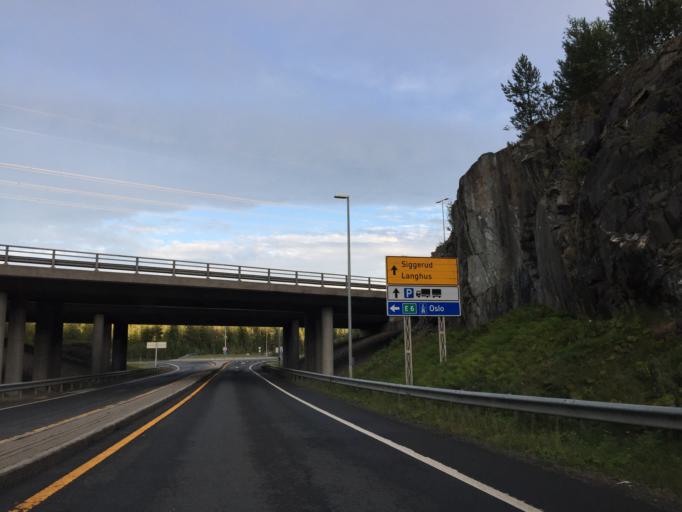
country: NO
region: Akershus
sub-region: Oppegard
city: Kolbotn
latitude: 59.7842
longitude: 10.8381
